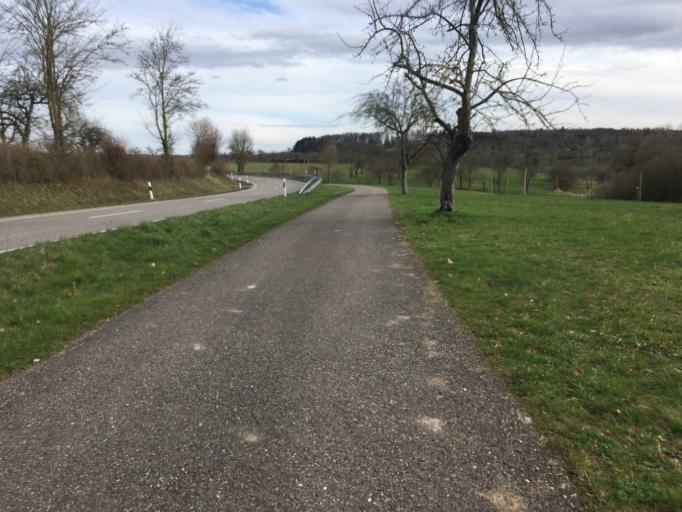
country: DE
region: Baden-Wuerttemberg
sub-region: Regierungsbezirk Stuttgart
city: Neuenstadt am Kocher
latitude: 49.2211
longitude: 9.3864
